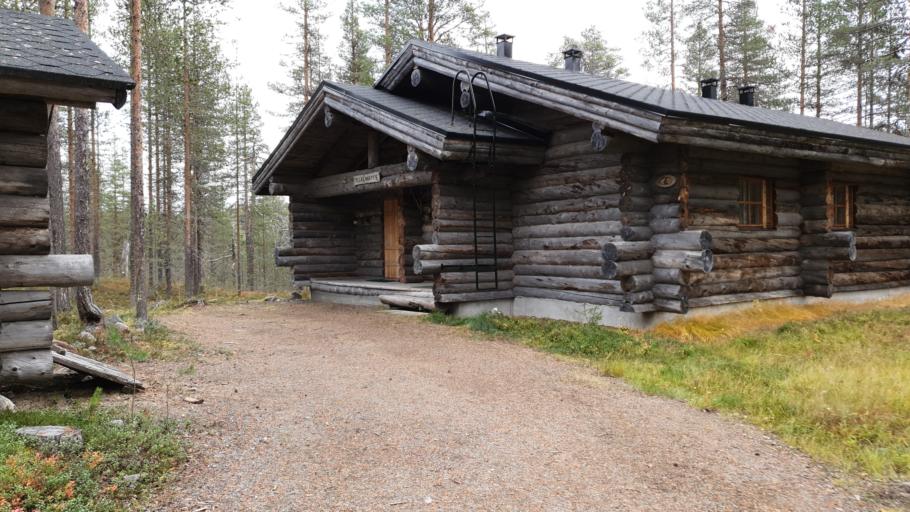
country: FI
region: Lapland
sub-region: Tunturi-Lappi
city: Kolari
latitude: 67.5966
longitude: 24.1152
